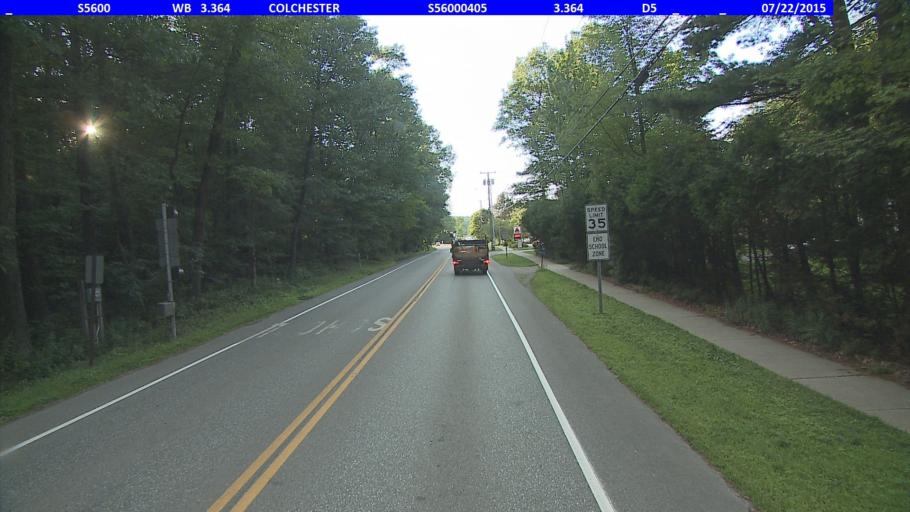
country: US
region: Vermont
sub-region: Chittenden County
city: Winooski
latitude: 44.5428
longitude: -73.2136
